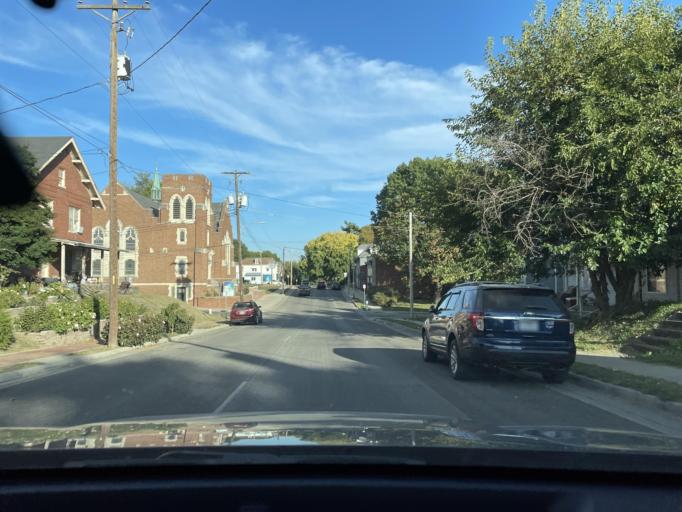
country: US
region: Missouri
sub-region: Buchanan County
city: Saint Joseph
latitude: 39.7683
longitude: -94.8357
